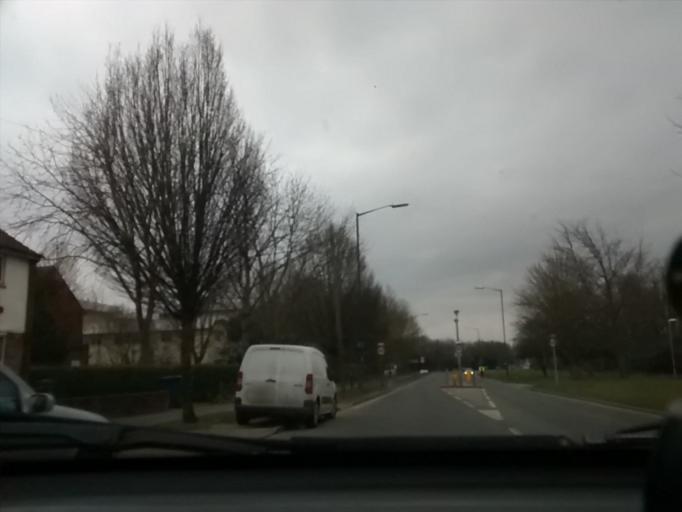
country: GB
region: England
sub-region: Cambridgeshire
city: Cambridge
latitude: 52.2079
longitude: 0.1635
